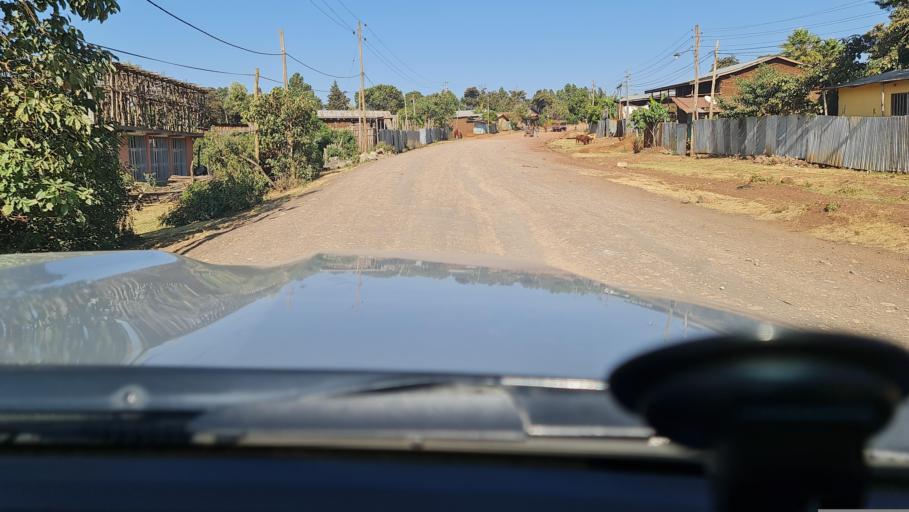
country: ET
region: Oromiya
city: Waliso
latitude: 8.6052
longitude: 37.9257
